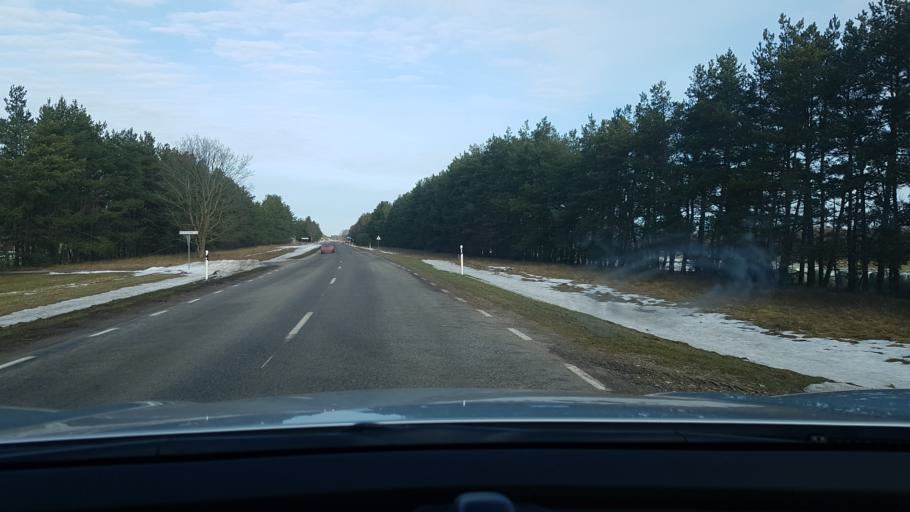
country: EE
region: Saare
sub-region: Kuressaare linn
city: Kuressaare
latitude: 58.5104
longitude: 22.7061
